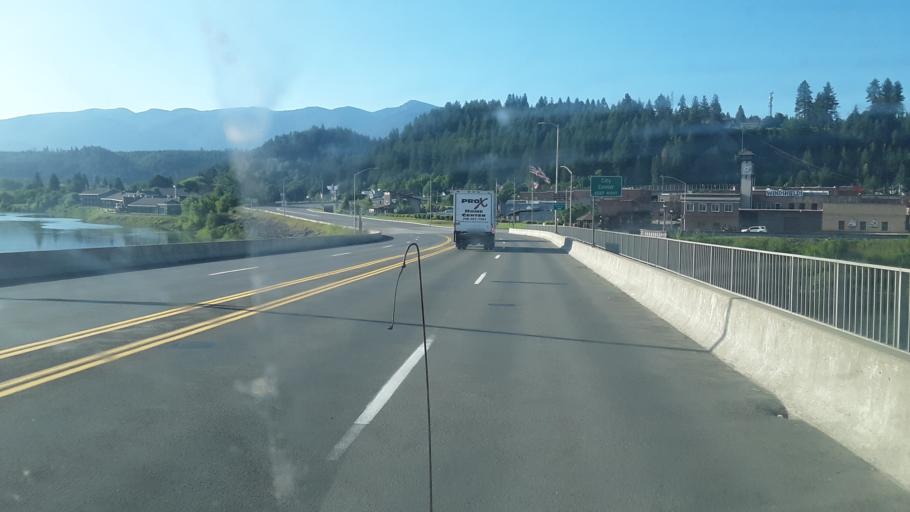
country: US
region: Idaho
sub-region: Boundary County
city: Bonners Ferry
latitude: 48.6993
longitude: -116.3131
